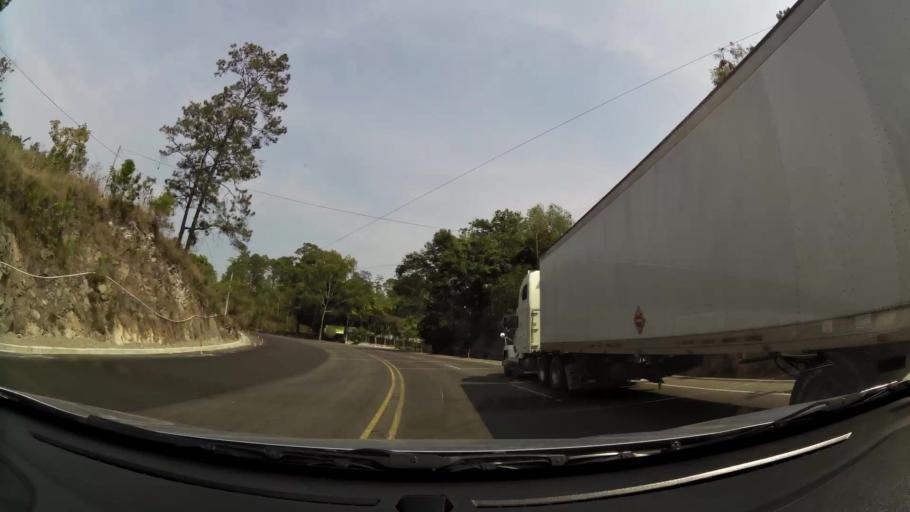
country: HN
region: Comayagua
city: Potrerillos
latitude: 14.5400
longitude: -87.8181
